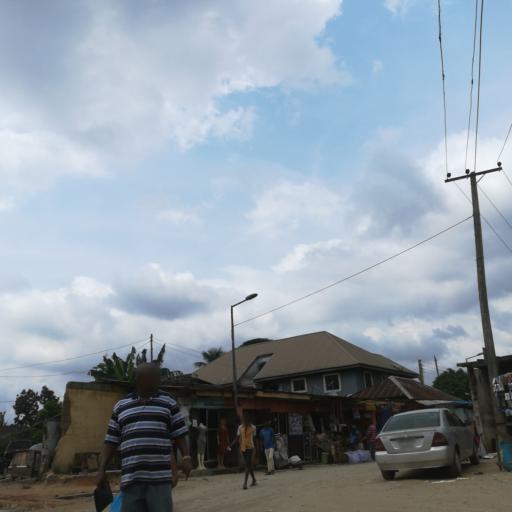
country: NG
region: Rivers
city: Port Harcourt
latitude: 4.8499
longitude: 7.0634
